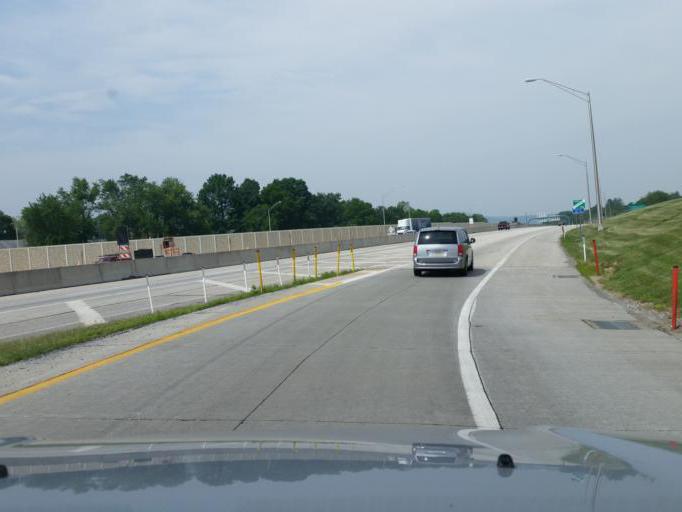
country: US
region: Pennsylvania
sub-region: Dauphin County
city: Highspire
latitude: 40.2152
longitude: -76.7872
